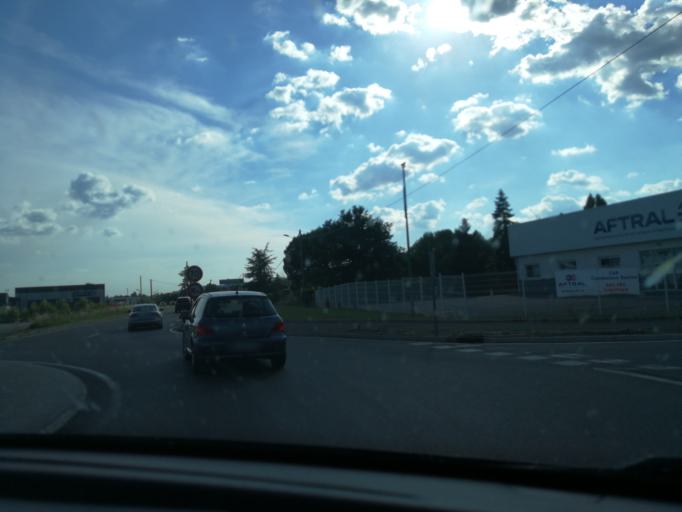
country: FR
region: Midi-Pyrenees
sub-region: Departement du Tarn
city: Cagnac-les-Mines
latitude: 43.9615
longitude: 2.1674
